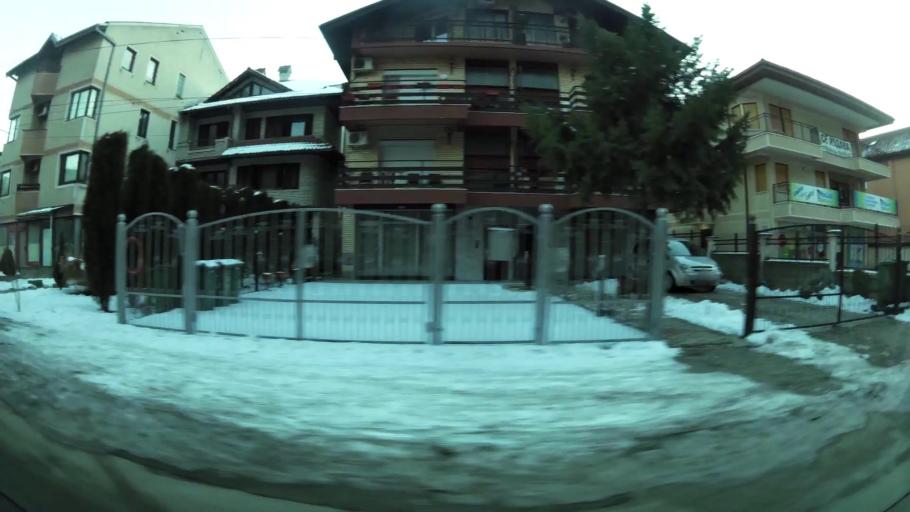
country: MK
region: Karpos
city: Skopje
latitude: 41.9914
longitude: 21.4176
